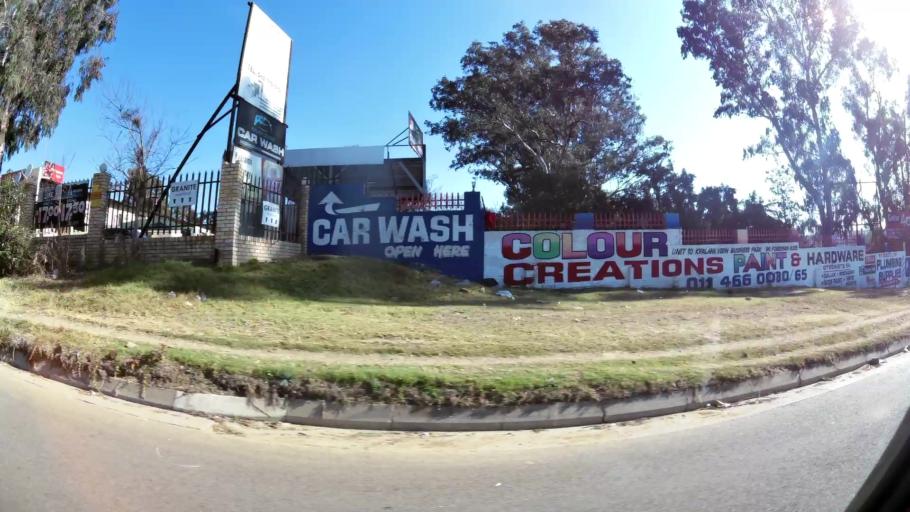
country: ZA
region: Gauteng
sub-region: City of Johannesburg Metropolitan Municipality
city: Midrand
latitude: -26.0068
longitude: 28.0789
